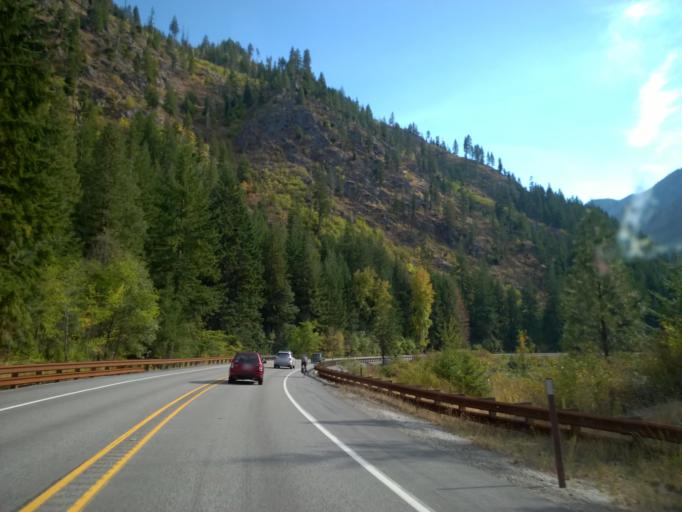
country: US
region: Washington
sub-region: Chelan County
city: Leavenworth
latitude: 47.6406
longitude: -120.7201
